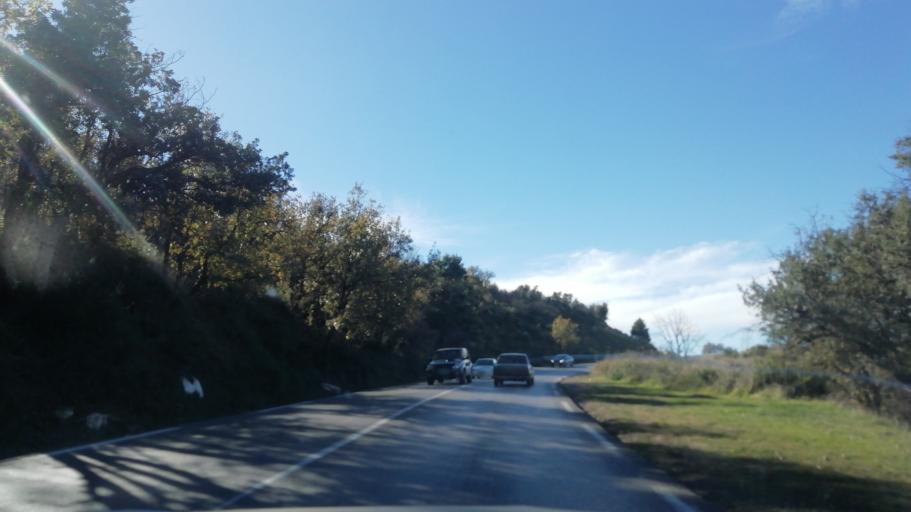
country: DZ
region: Tlemcen
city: Mansoura
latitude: 34.8389
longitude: -1.3692
